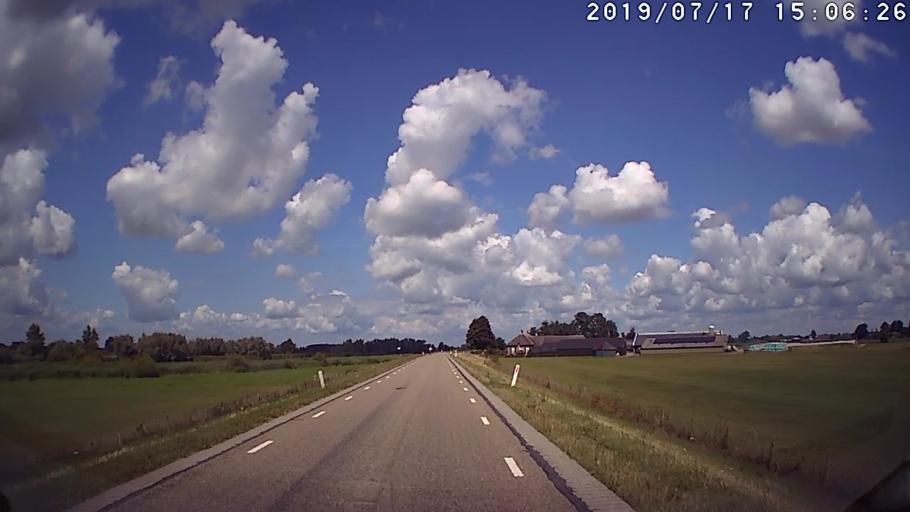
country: NL
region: Overijssel
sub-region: Gemeente Kampen
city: Kampen
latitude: 52.5136
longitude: 5.9790
